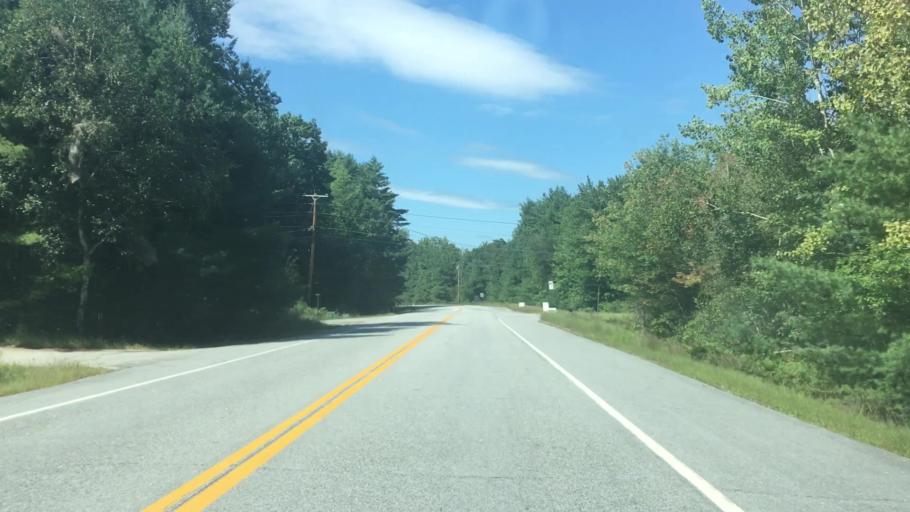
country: US
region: Maine
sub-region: Kennebec County
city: Monmouth
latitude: 44.1918
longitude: -69.9678
